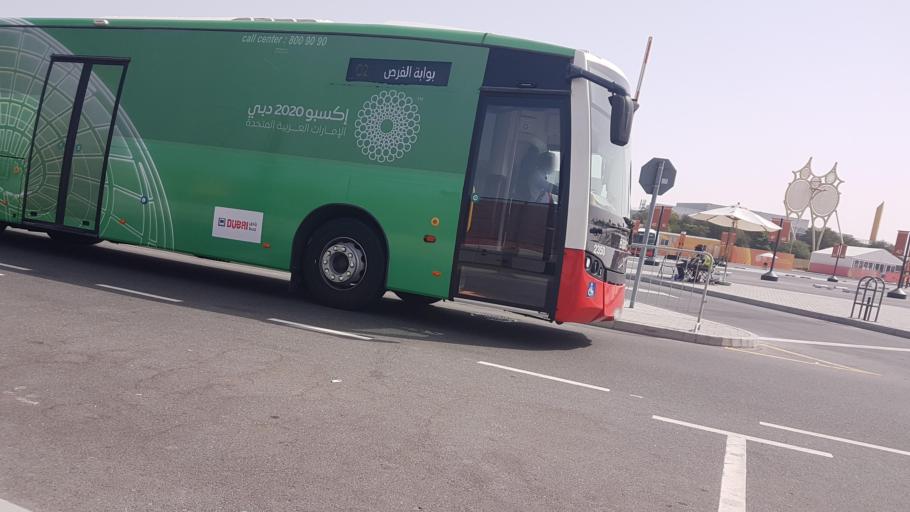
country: AE
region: Dubai
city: Dubai
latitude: 24.9660
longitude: 55.1563
